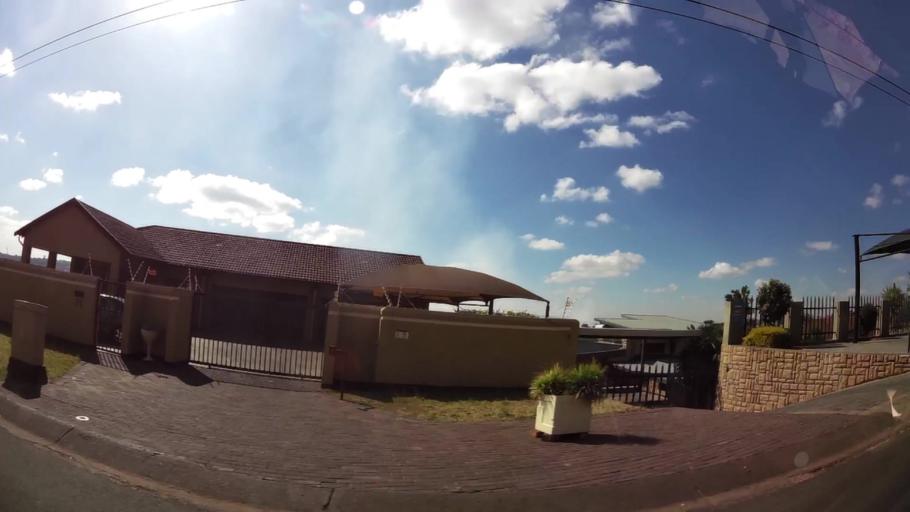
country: ZA
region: Gauteng
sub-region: City of Johannesburg Metropolitan Municipality
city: Roodepoort
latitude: -26.1147
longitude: 27.8445
